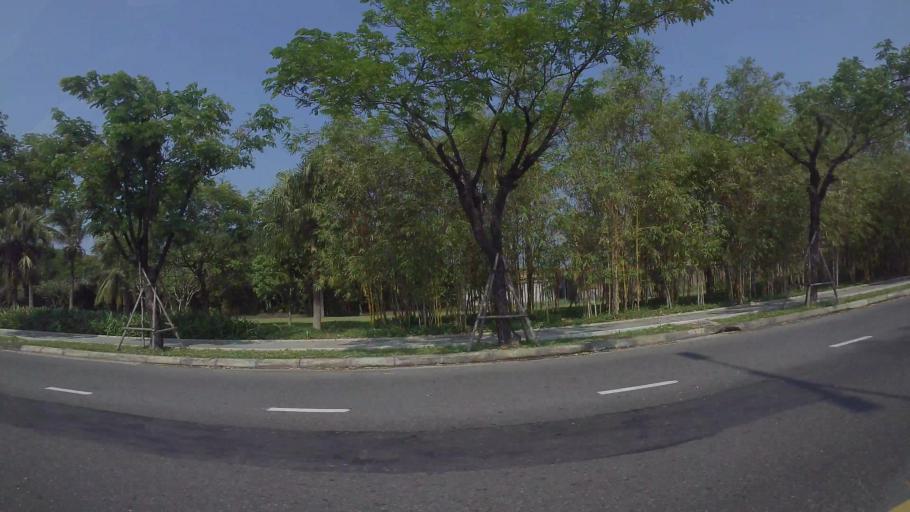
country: VN
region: Da Nang
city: Ngu Hanh Son
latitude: 16.0112
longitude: 108.2629
